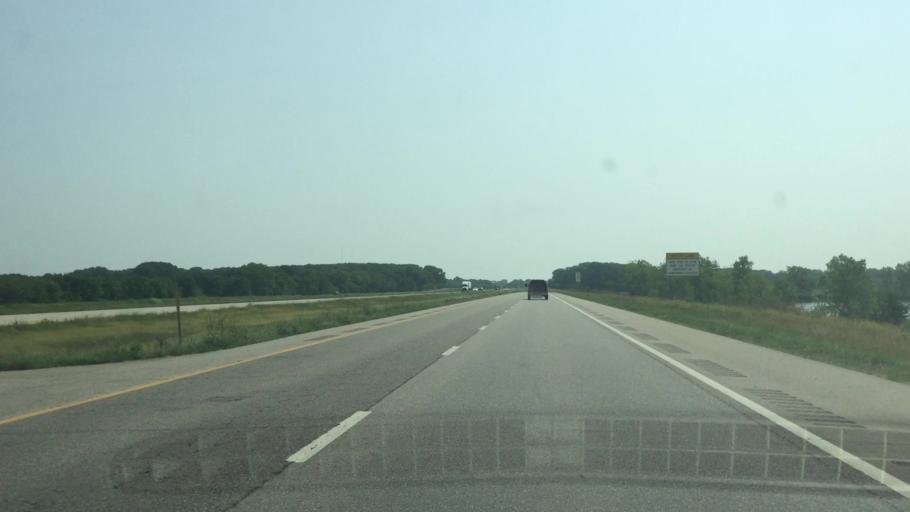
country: US
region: Kansas
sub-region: Lyon County
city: Emporia
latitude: 38.4108
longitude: -96.1300
